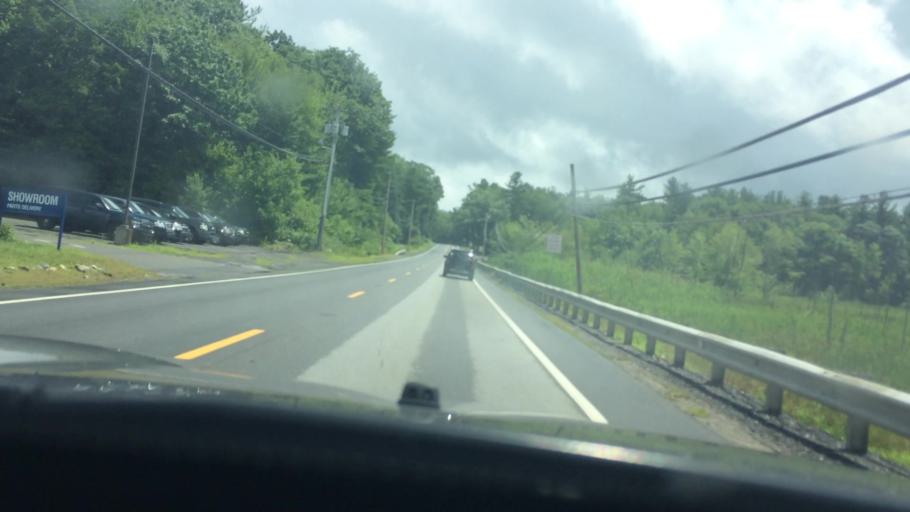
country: US
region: Massachusetts
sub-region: Worcester County
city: Phillipston
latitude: 42.5721
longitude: -72.1592
